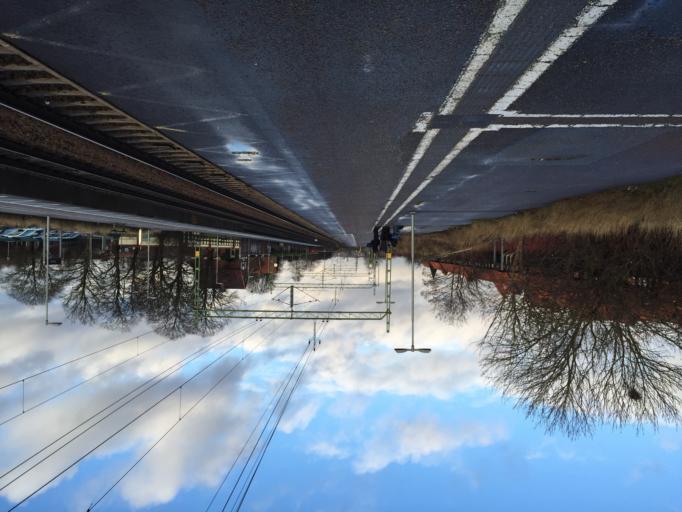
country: SE
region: Skane
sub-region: Staffanstorps Kommun
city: Hjaerup
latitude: 55.6739
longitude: 13.1362
